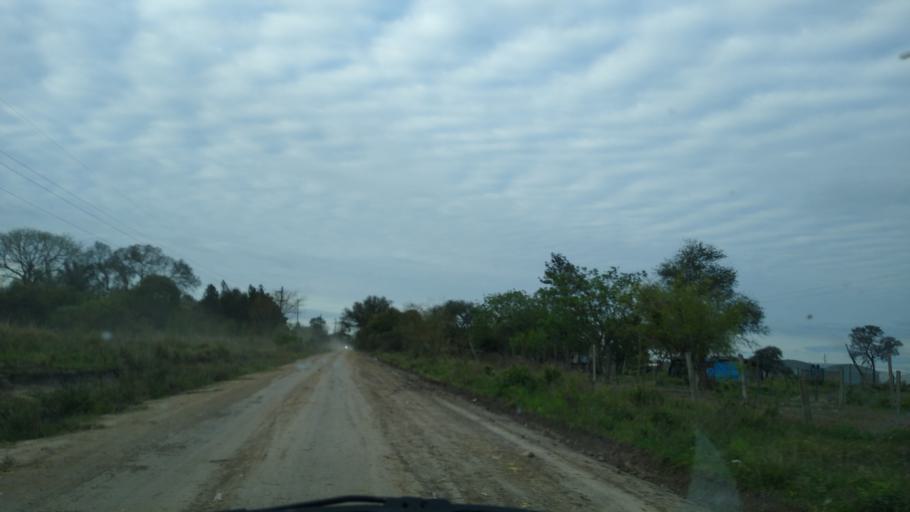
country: AR
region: Chaco
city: Fontana
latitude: -27.3833
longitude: -59.0418
